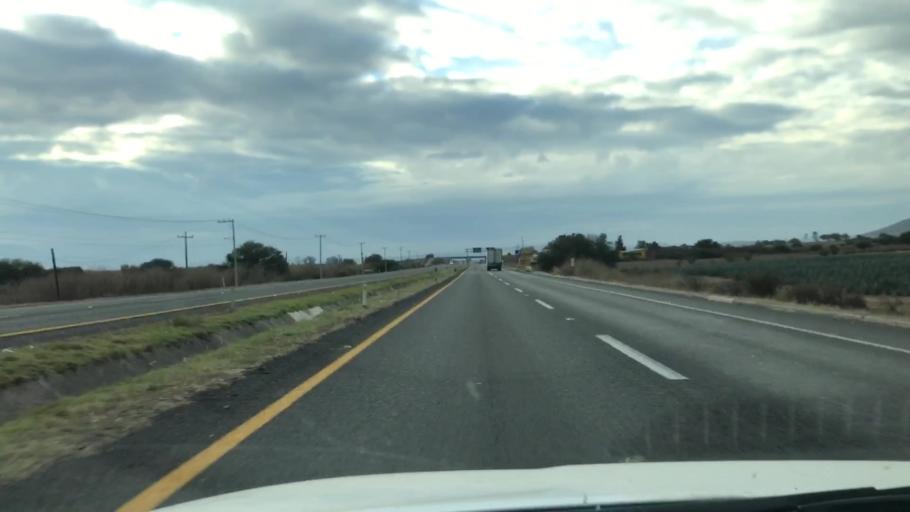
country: MX
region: Guanajuato
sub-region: Penjamo
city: Mezquite de Luna
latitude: 20.3785
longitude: -101.8548
